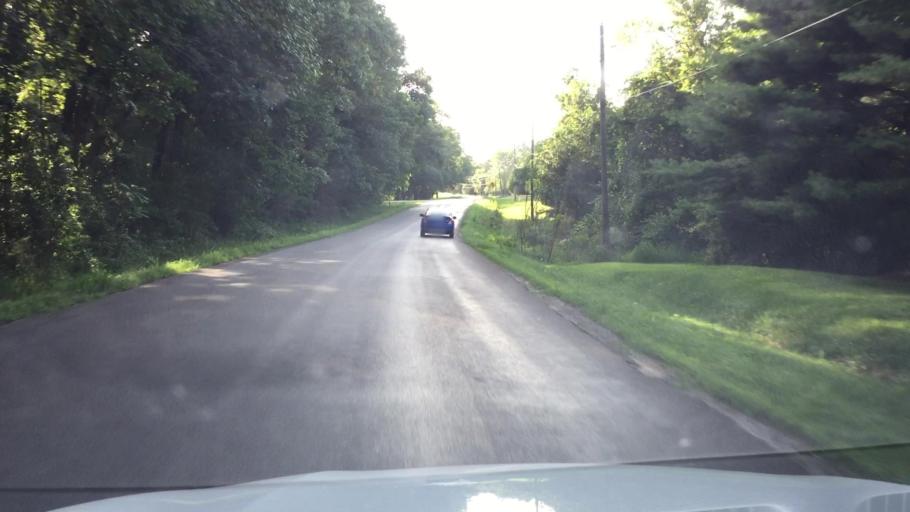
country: US
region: Iowa
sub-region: Linn County
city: Ely
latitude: 41.8305
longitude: -91.6284
